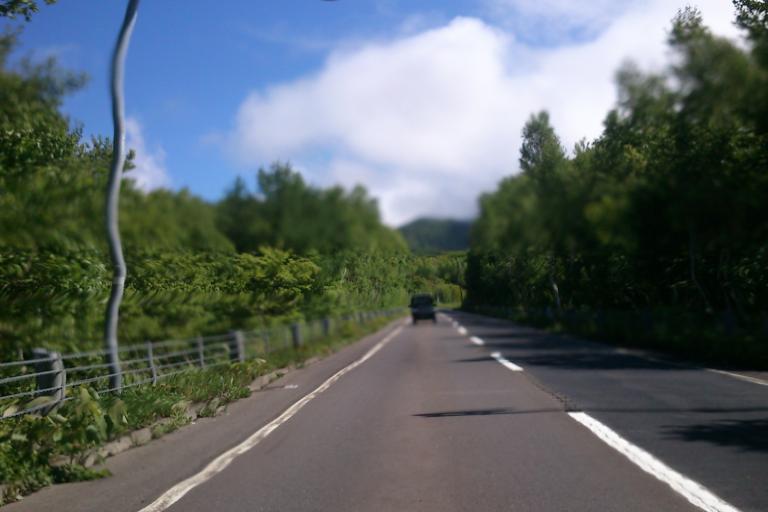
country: JP
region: Hokkaido
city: Ishikari
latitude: 43.5085
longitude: 141.3738
